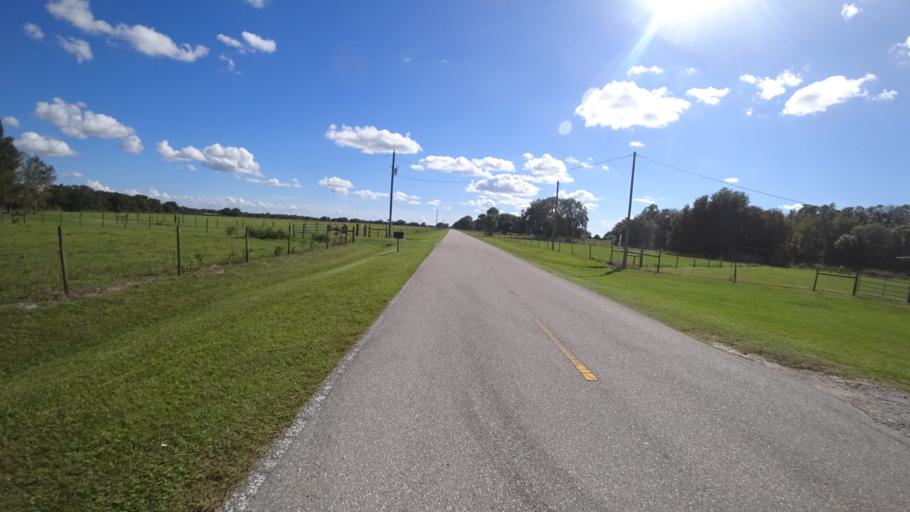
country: US
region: Florida
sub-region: Sarasota County
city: North Port
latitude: 27.2043
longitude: -82.1222
